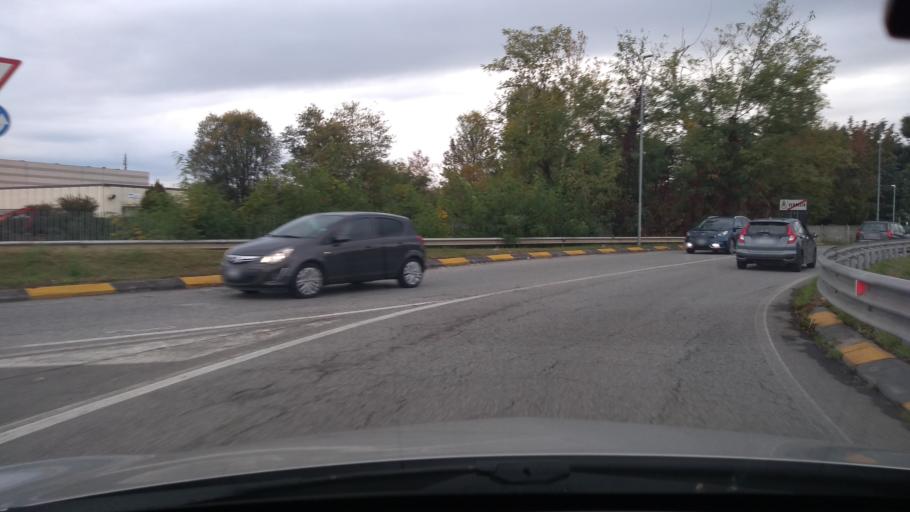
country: IT
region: Lombardy
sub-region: Provincia di Bergamo
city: Levate
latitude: 45.6167
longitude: 9.6333
